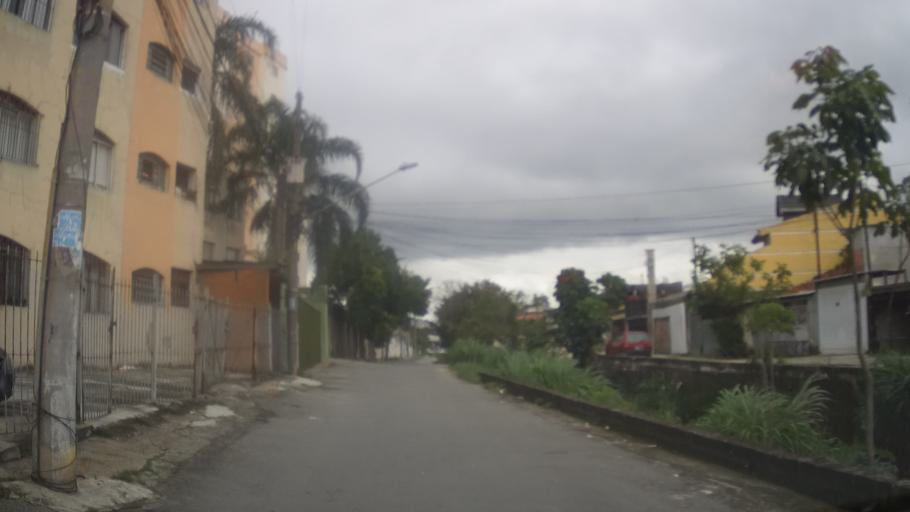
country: BR
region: Sao Paulo
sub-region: Guarulhos
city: Guarulhos
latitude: -23.4527
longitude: -46.5221
